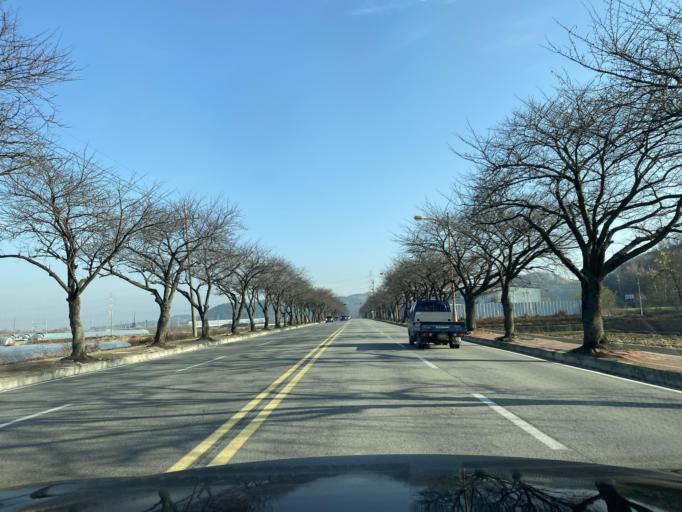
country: KR
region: Chungcheongnam-do
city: Yesan
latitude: 36.7291
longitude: 126.8562
